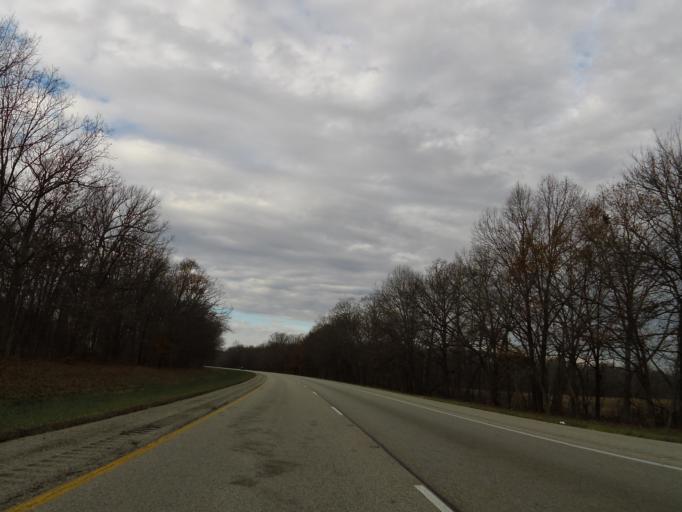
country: US
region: Illinois
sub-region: Washington County
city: Nashville
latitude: 38.3923
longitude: -89.3127
